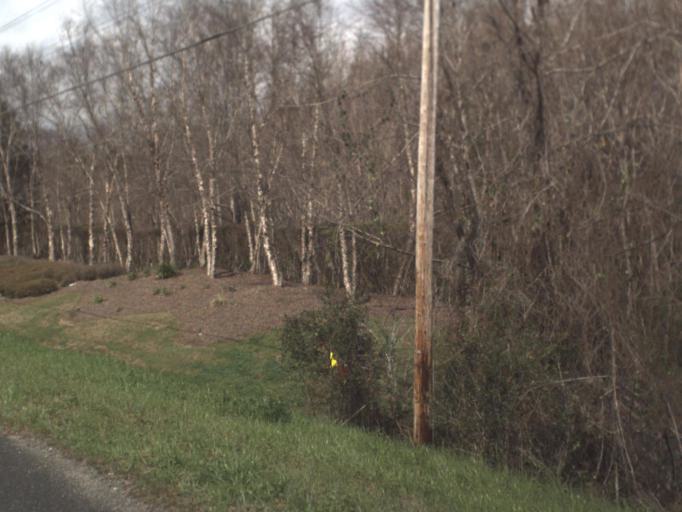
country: US
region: Florida
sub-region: Leon County
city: Tallahassee
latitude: 30.4222
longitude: -84.1672
